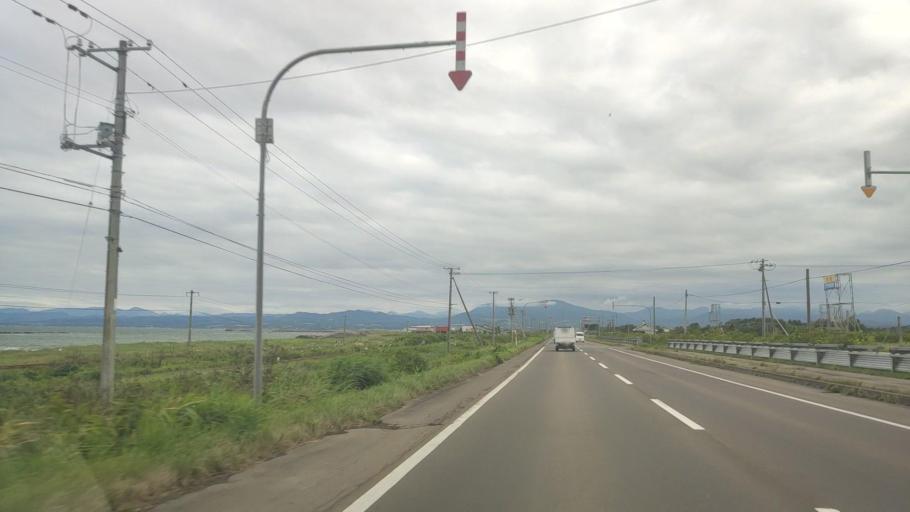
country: JP
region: Hokkaido
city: Nanae
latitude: 42.3236
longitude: 140.2761
